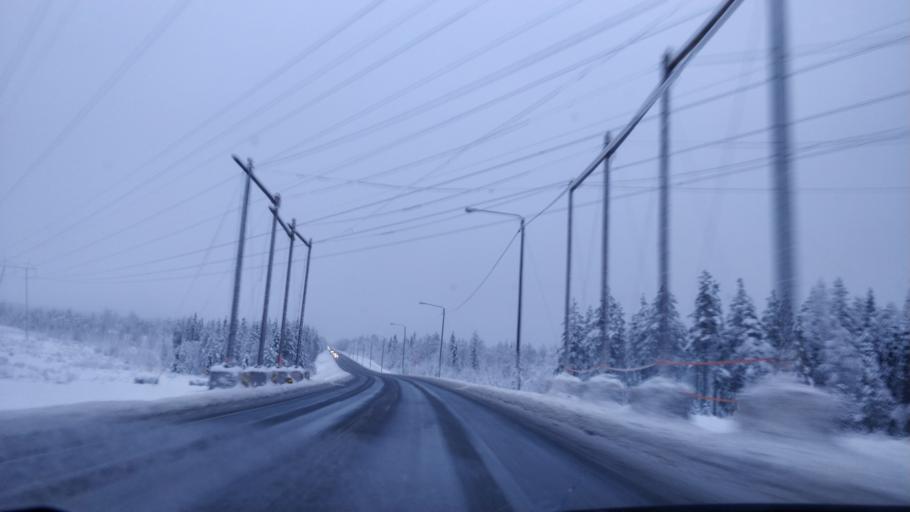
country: FI
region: Lapland
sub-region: Rovaniemi
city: Rovaniemi
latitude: 66.4442
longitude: 25.5594
